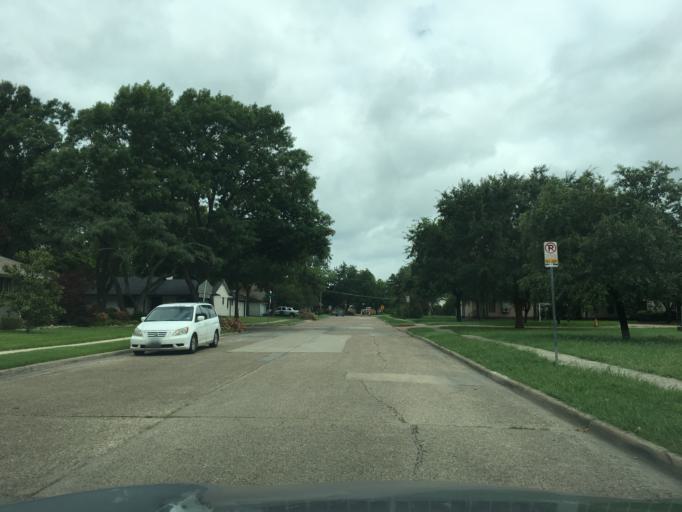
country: US
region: Texas
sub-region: Dallas County
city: Highland Park
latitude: 32.8575
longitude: -96.7411
